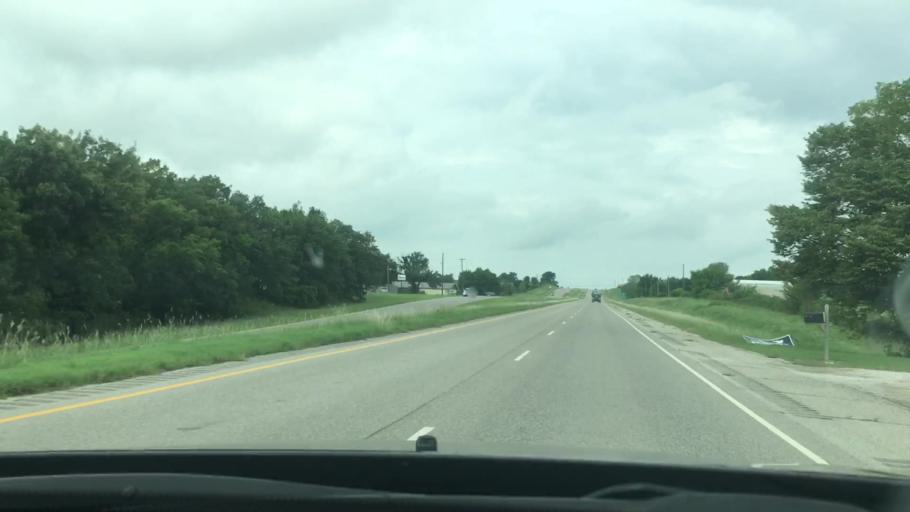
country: US
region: Oklahoma
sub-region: Carter County
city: Wilson
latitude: 34.1731
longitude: -97.4523
